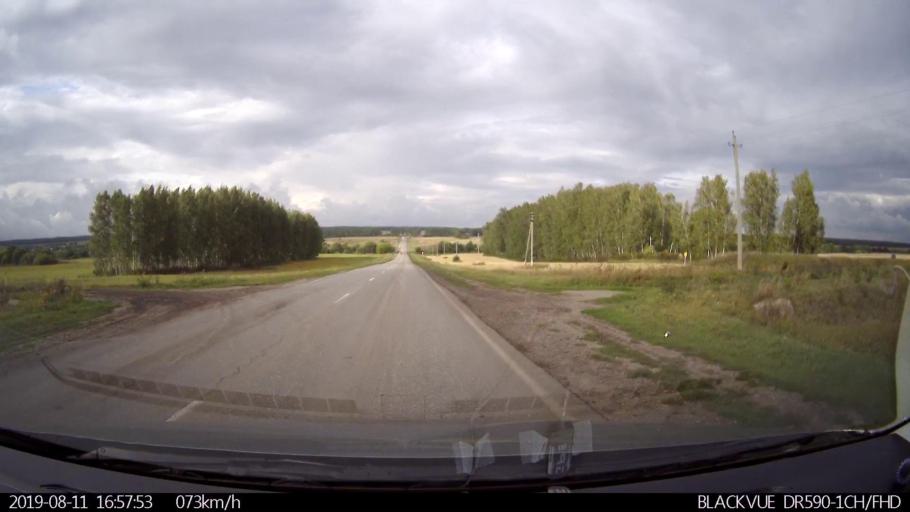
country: RU
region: Ulyanovsk
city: Mayna
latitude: 54.3024
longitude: 47.6547
